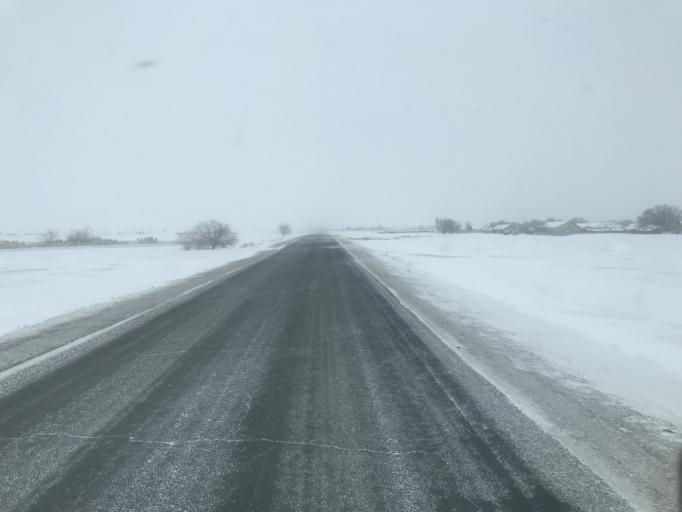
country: KZ
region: Batys Qazaqstan
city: Chapaev
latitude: 50.5033
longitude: 51.0532
